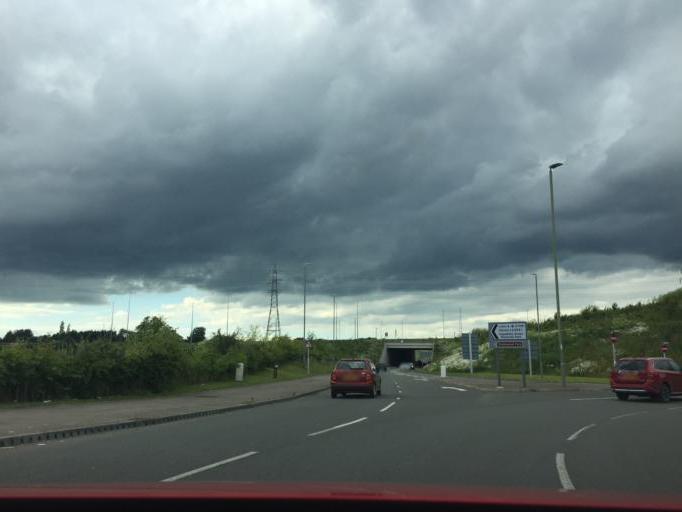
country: GB
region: England
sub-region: Luton
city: Luton
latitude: 51.8563
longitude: -0.4158
